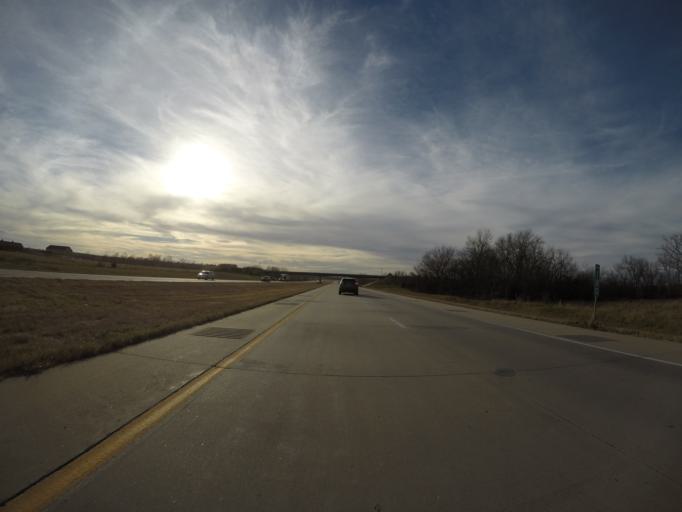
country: US
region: Kansas
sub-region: Franklin County
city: Ottawa
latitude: 38.5602
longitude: -95.3211
